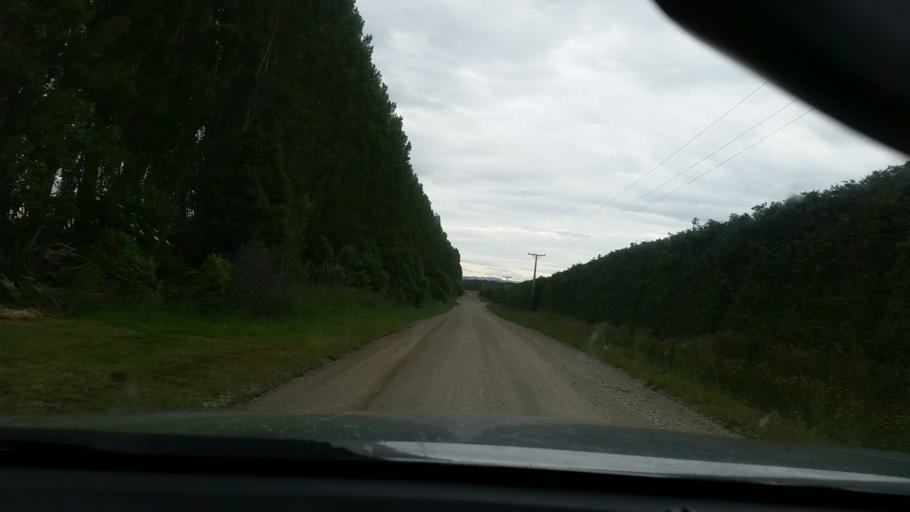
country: NZ
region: Southland
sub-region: Gore District
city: Gore
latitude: -46.2841
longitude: 168.7878
